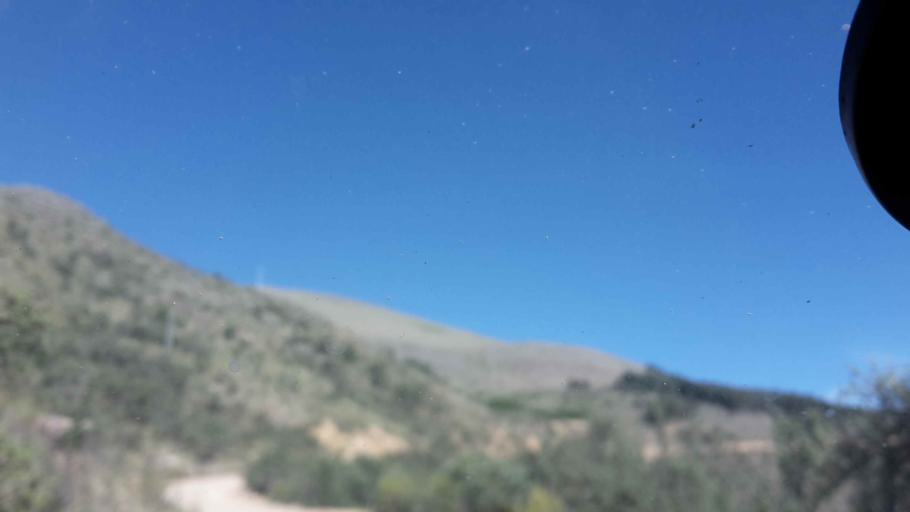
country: BO
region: Cochabamba
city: Arani
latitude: -17.6755
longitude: -65.7274
